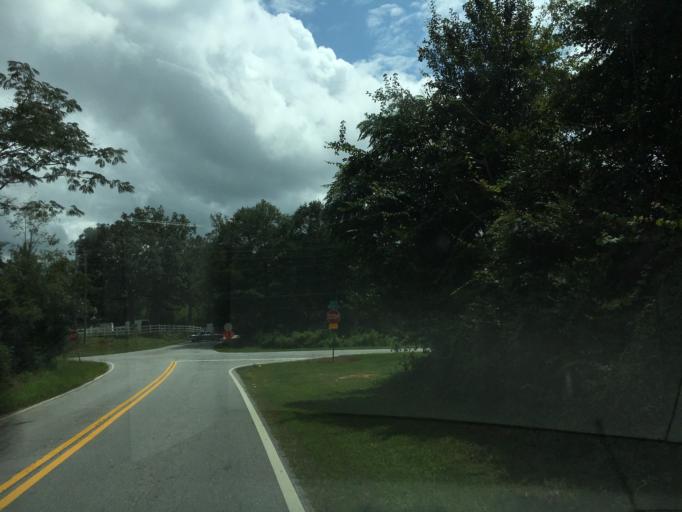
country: US
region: Georgia
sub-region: Rockdale County
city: Lakeview Estates
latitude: 33.6959
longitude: -84.0413
